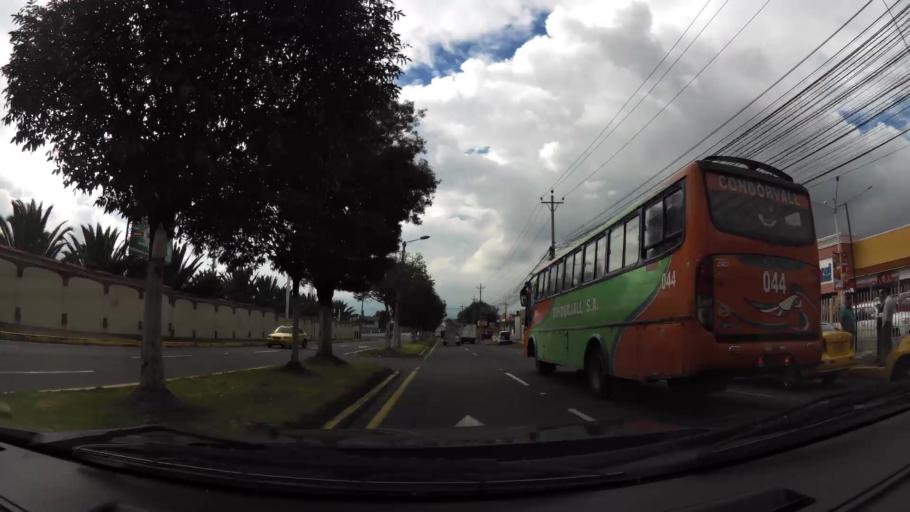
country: EC
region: Pichincha
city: Sangolqui
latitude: -0.3149
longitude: -78.4507
